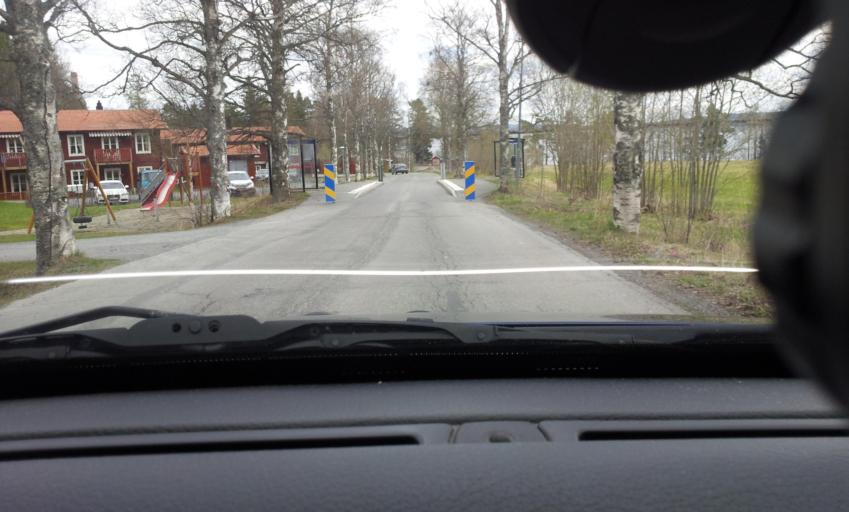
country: SE
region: Jaemtland
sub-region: OEstersunds Kommun
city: Ostersund
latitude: 63.1666
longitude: 14.5904
